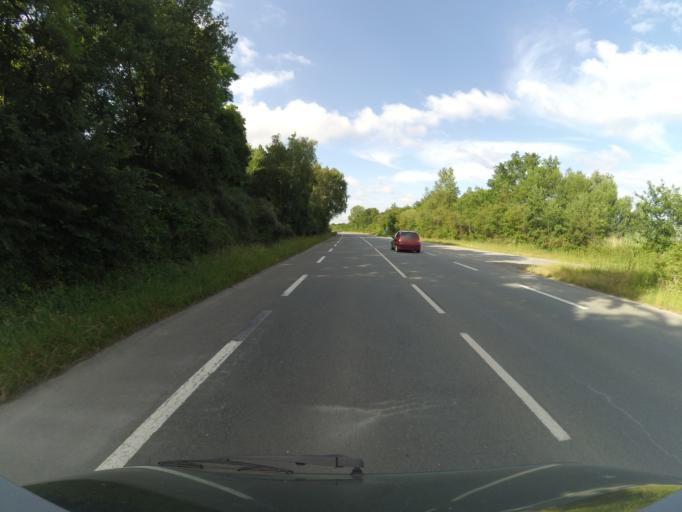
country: FR
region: Poitou-Charentes
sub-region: Departement de la Charente-Maritime
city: Le Gua
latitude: 45.7684
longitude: -0.9380
